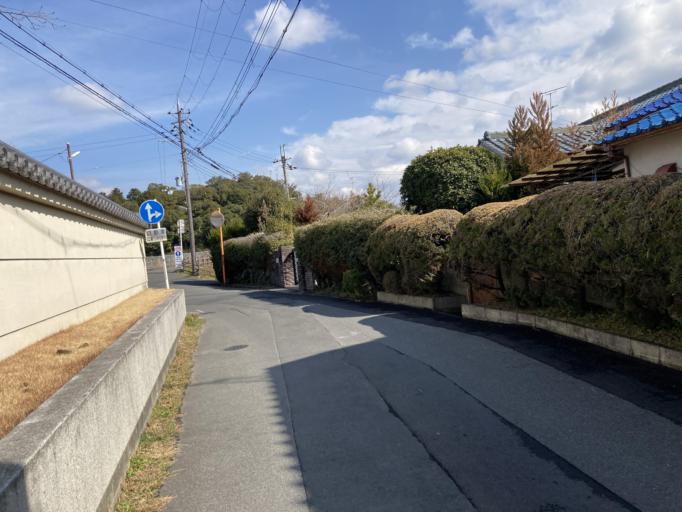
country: JP
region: Nara
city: Nara-shi
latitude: 34.6969
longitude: 135.8067
